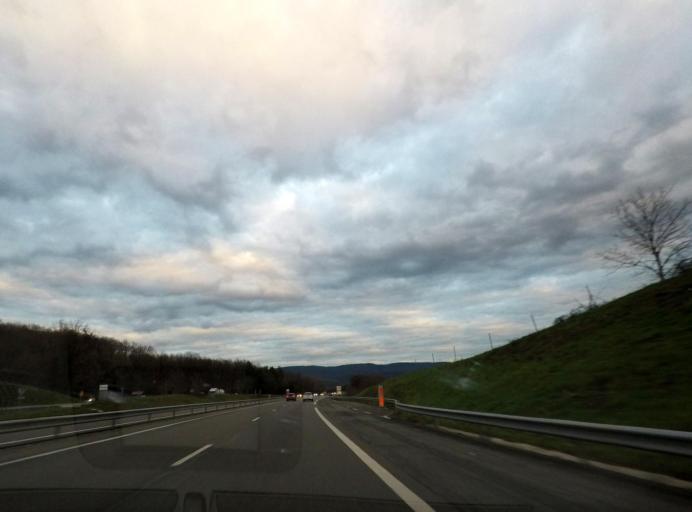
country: FR
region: Rhone-Alpes
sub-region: Departement de l'Ain
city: Neuville-sur-Ain
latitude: 46.0881
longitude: 5.3779
